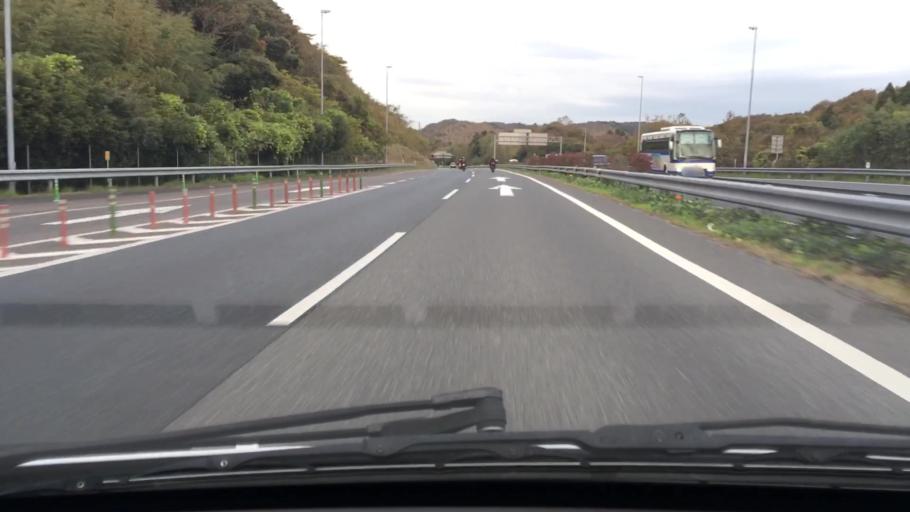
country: JP
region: Chiba
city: Kisarazu
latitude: 35.3565
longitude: 139.9516
